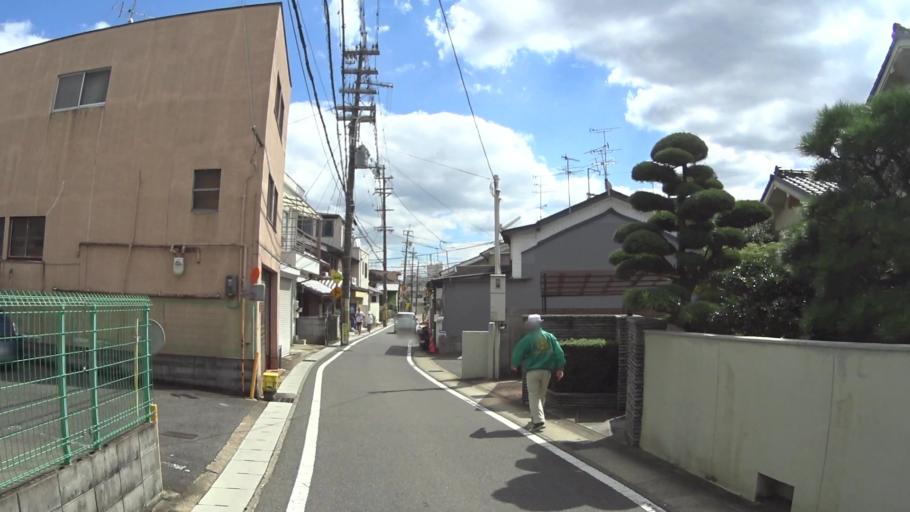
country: JP
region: Kyoto
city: Uji
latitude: 34.9155
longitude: 135.8012
